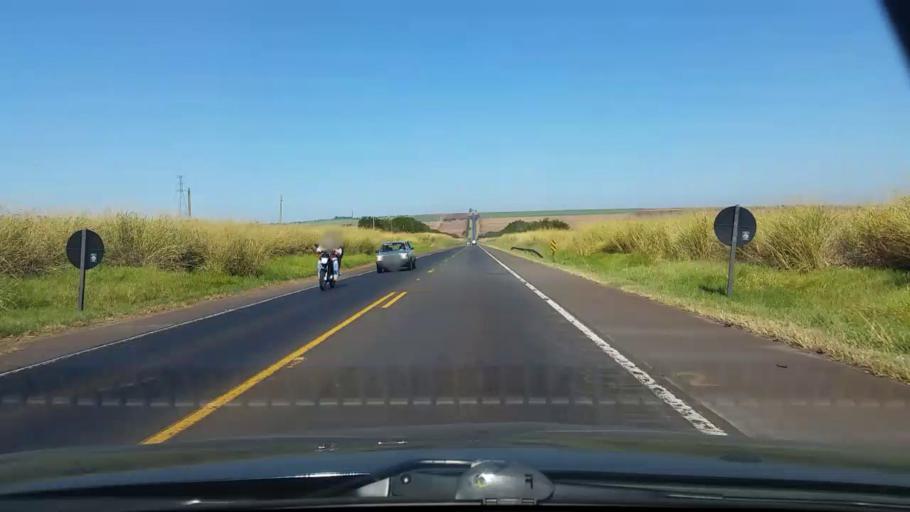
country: BR
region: Sao Paulo
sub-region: Jau
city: Jau
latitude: -22.3600
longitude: -48.5721
